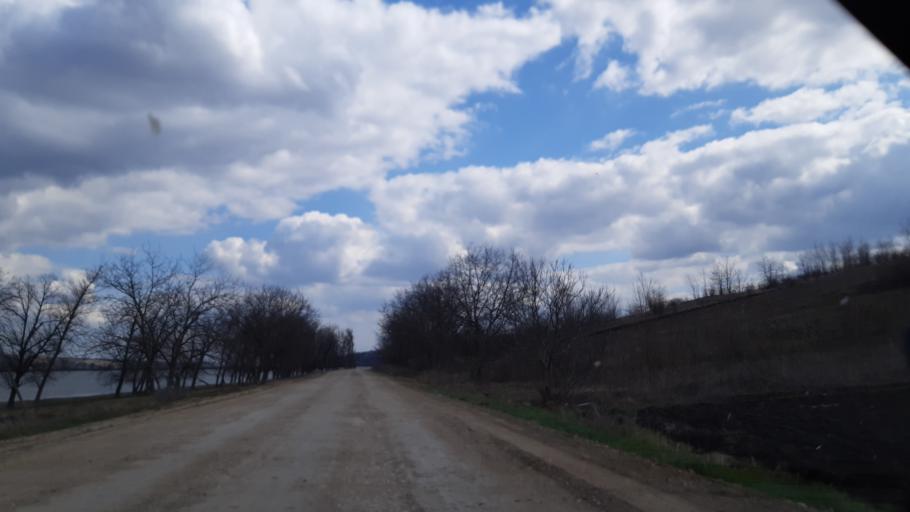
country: MD
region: Laloveni
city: Ialoveni
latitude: 46.8886
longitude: 28.7325
